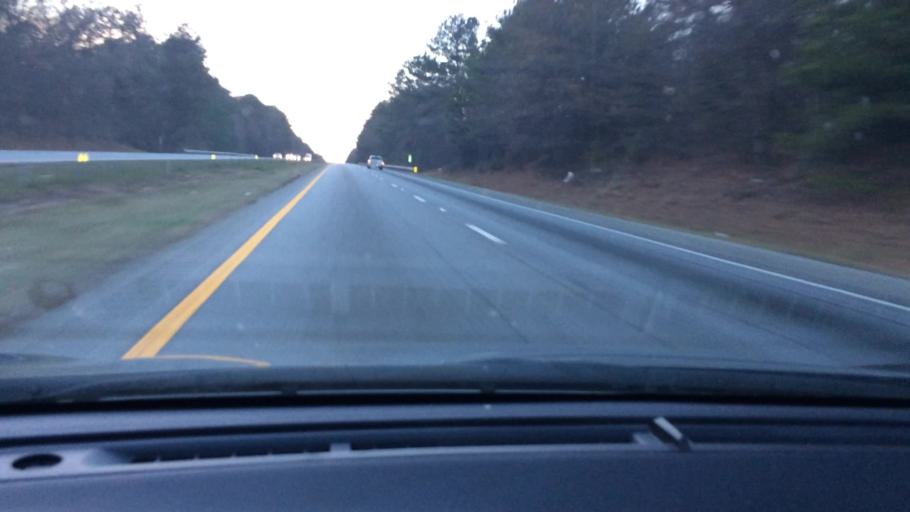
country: US
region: South Carolina
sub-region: Laurens County
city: Joanna
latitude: 34.4267
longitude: -81.7249
